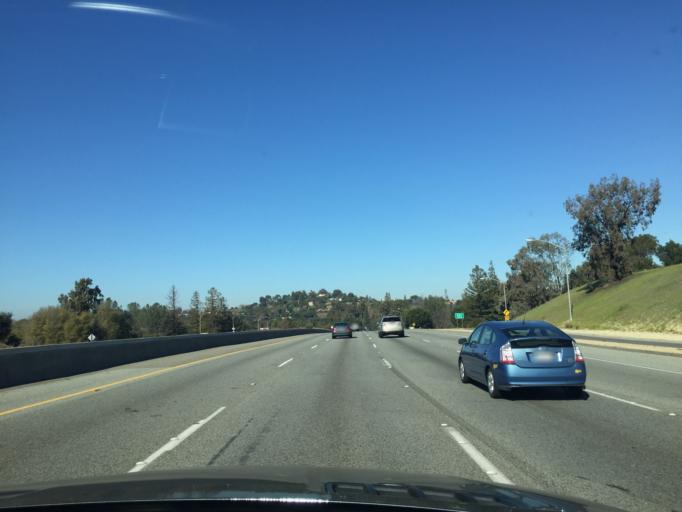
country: US
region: California
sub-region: Santa Clara County
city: Loyola
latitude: 37.3589
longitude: -122.1186
